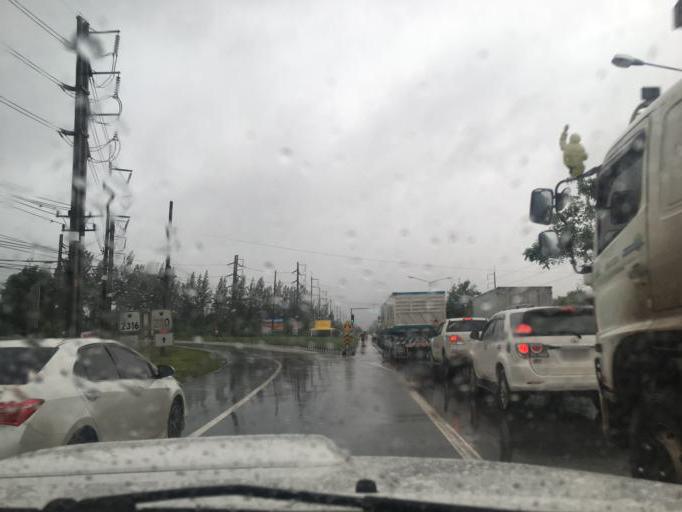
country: TH
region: Changwat Udon Thani
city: Udon Thani
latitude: 17.3713
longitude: 102.7229
